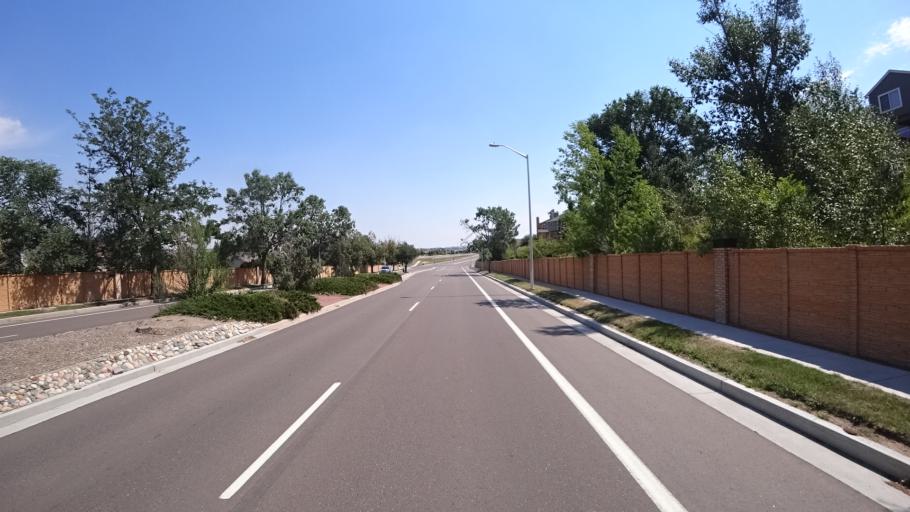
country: US
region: Colorado
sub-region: El Paso County
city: Cimarron Hills
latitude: 38.9250
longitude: -104.7579
